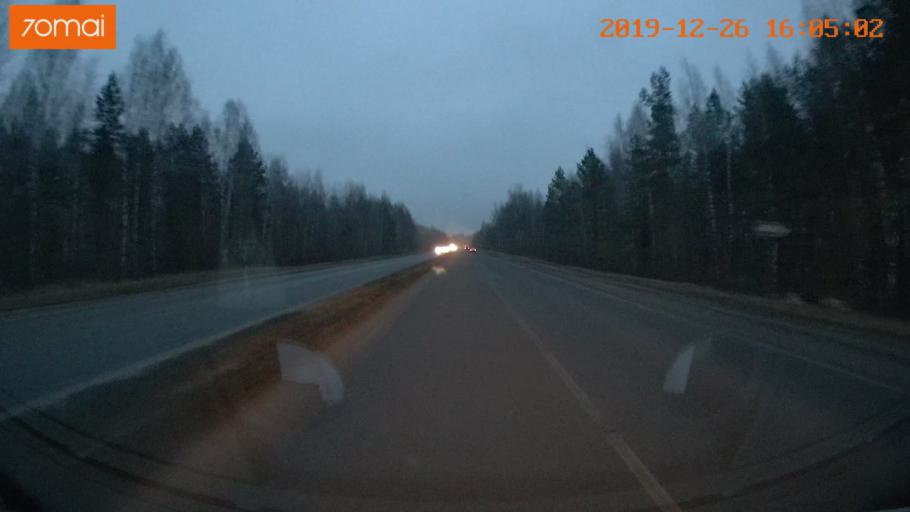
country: RU
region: Jaroslavl
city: Rybinsk
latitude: 58.0075
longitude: 38.8850
